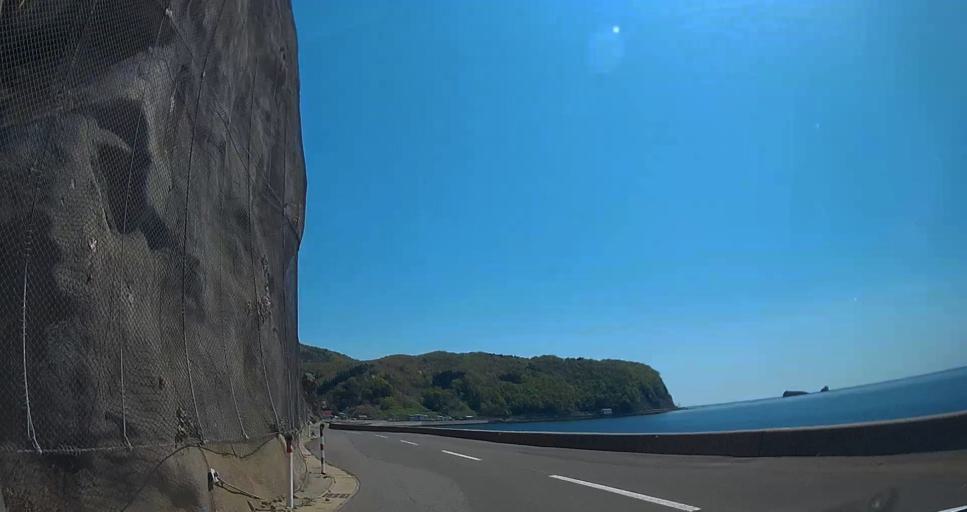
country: JP
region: Aomori
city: Aomori Shi
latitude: 41.1315
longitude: 140.7868
